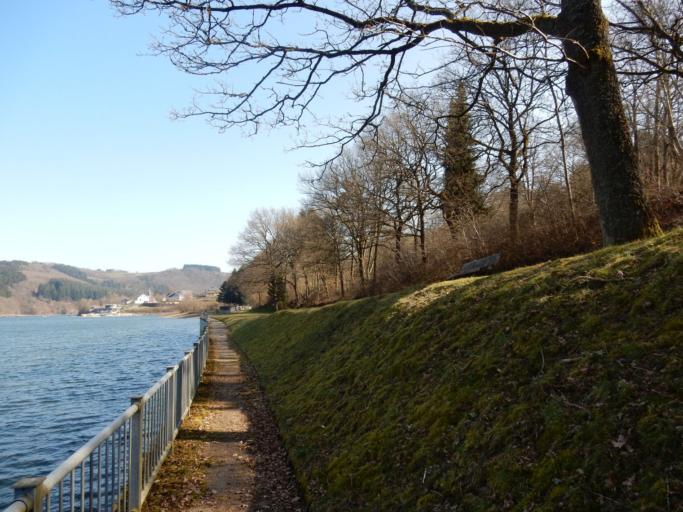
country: LU
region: Diekirch
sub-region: Canton de Wiltz
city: Bavigne
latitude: 49.9042
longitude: 5.8832
